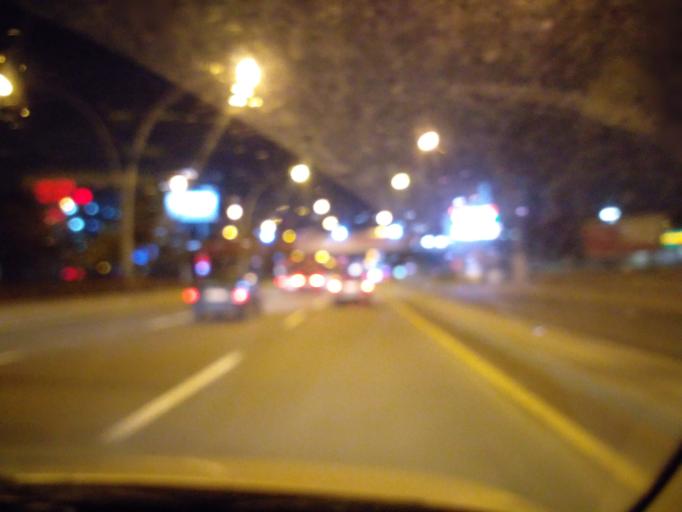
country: TR
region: Ankara
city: Batikent
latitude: 39.9068
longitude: 32.7431
